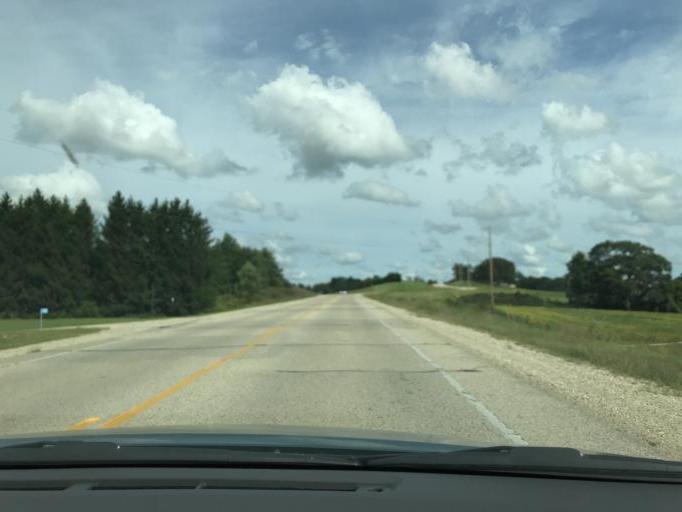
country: US
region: Wisconsin
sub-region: Racine County
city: Bohners Lake
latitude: 42.5987
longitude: -88.2226
